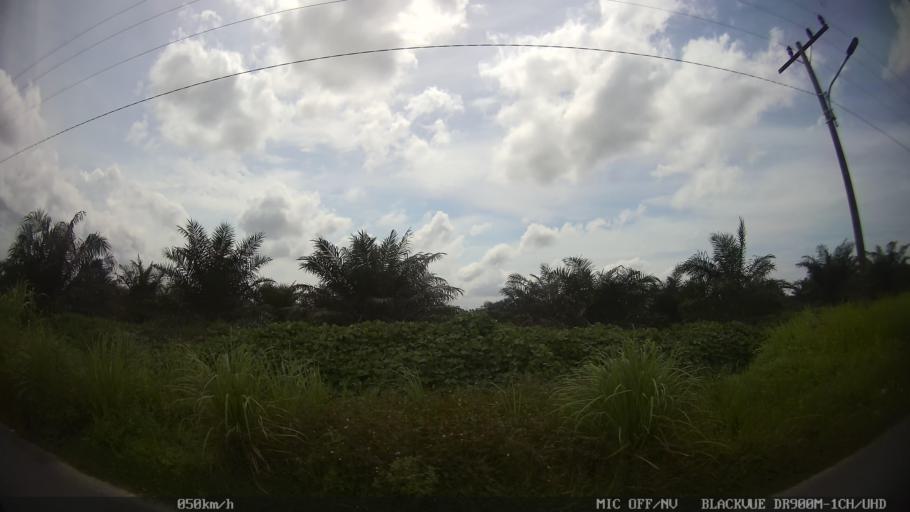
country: ID
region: North Sumatra
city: Percut
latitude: 3.5815
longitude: 98.8408
